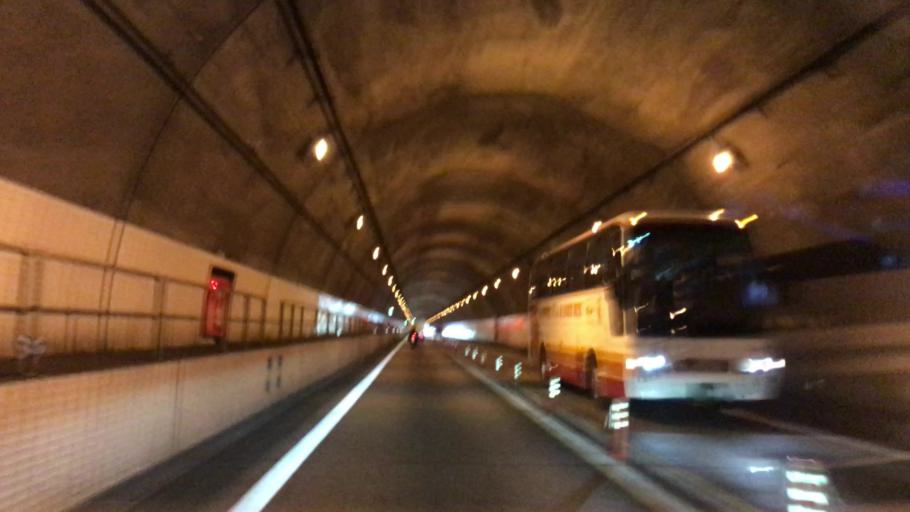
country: JP
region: Hokkaido
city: Chitose
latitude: 42.9160
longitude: 141.9448
